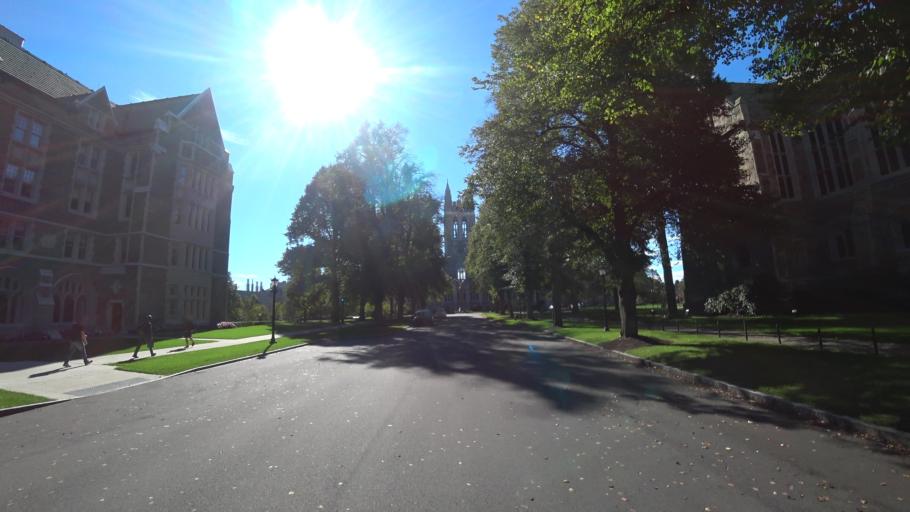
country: US
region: Massachusetts
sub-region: Middlesex County
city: Watertown
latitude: 42.3368
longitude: -71.1710
